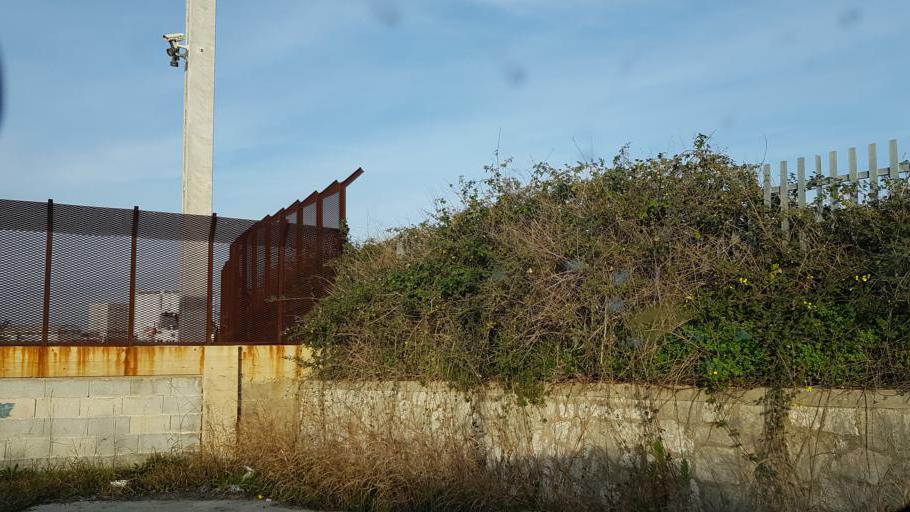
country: IT
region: Apulia
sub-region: Provincia di Brindisi
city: Brindisi
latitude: 40.6332
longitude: 17.9507
